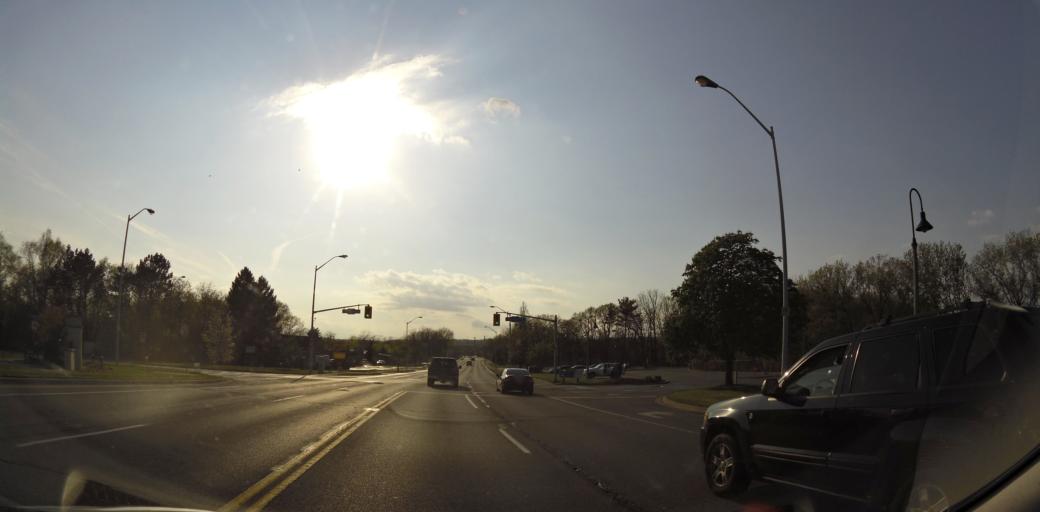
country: CA
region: Ontario
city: Hamilton
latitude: 43.2909
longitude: -79.8780
